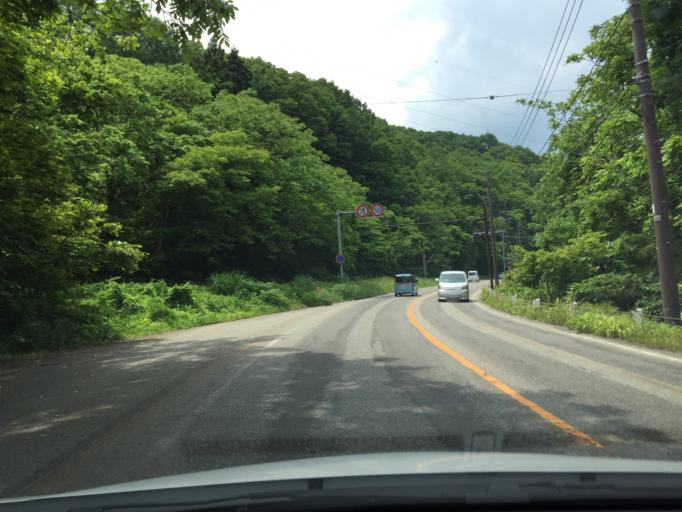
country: JP
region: Fukushima
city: Inawashiro
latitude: 37.6070
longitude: 140.1230
